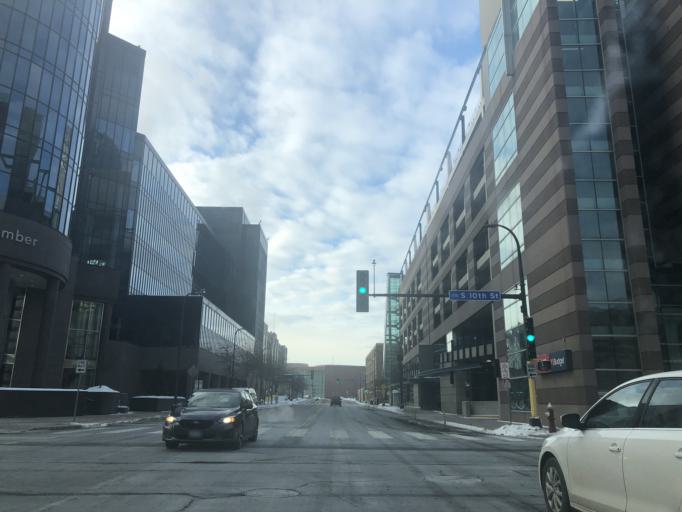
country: US
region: Minnesota
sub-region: Hennepin County
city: Minneapolis
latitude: 44.9724
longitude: -93.2705
